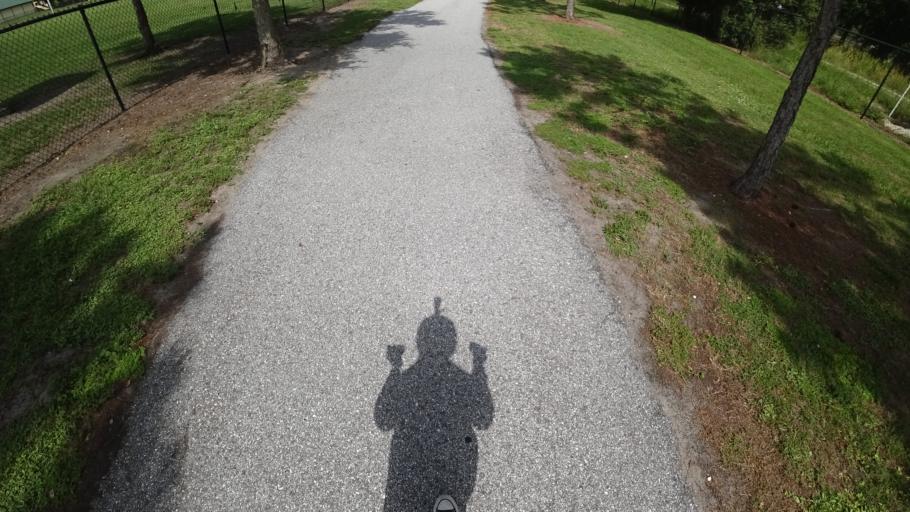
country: US
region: Florida
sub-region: Manatee County
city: Samoset
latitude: 27.4615
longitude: -82.4700
